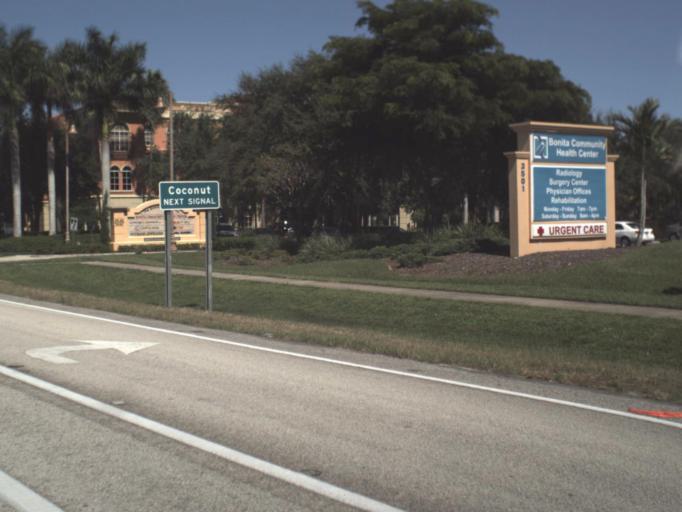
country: US
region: Florida
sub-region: Lee County
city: Estero
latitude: 26.3947
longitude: -81.8104
